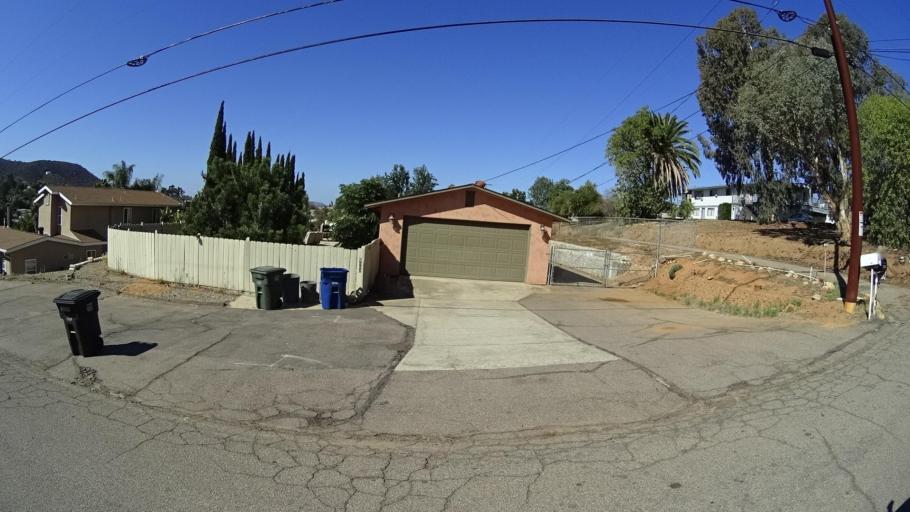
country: US
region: California
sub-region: San Diego County
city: Winter Gardens
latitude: 32.8474
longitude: -116.9382
